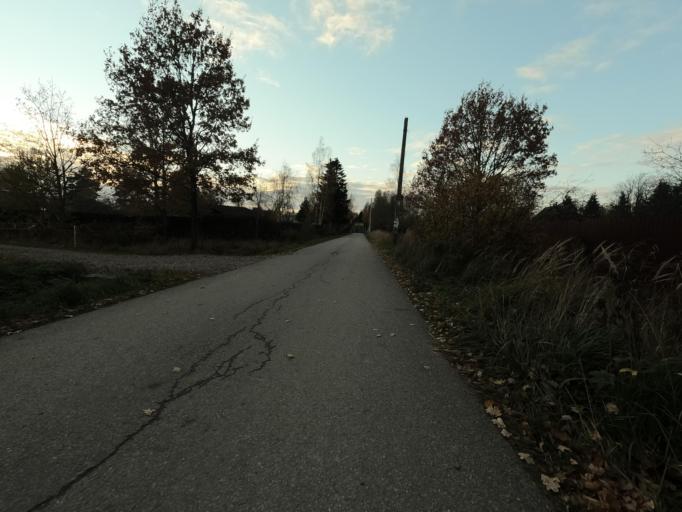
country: RU
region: Leningrad
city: Mga
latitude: 59.7765
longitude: 31.2083
